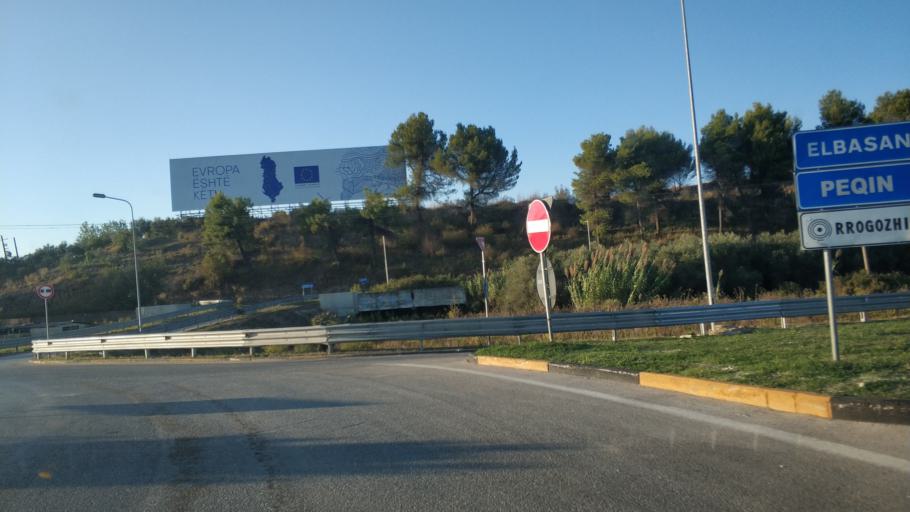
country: AL
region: Tirane
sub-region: Rrethi i Kavajes
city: Gose e Madhe
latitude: 41.0726
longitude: 19.6377
